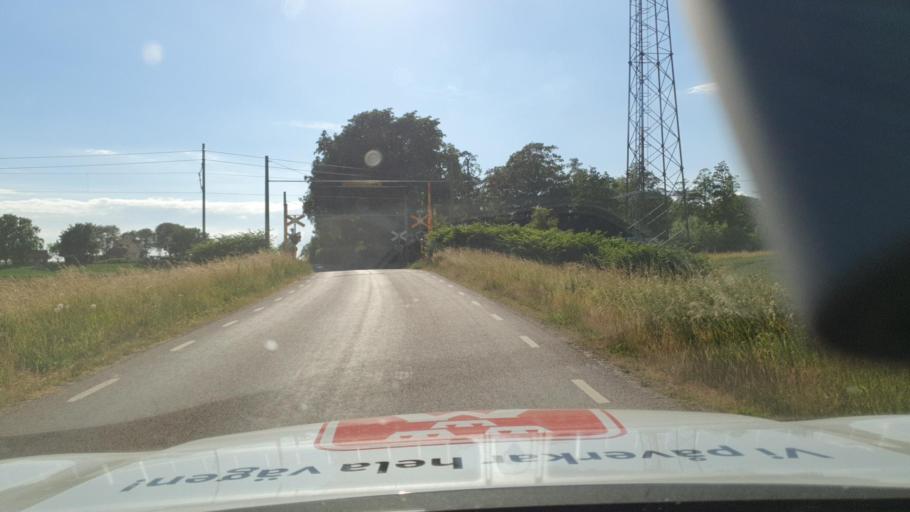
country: SE
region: Skane
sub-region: Ystads Kommun
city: Ystad
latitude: 55.4469
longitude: 13.7109
